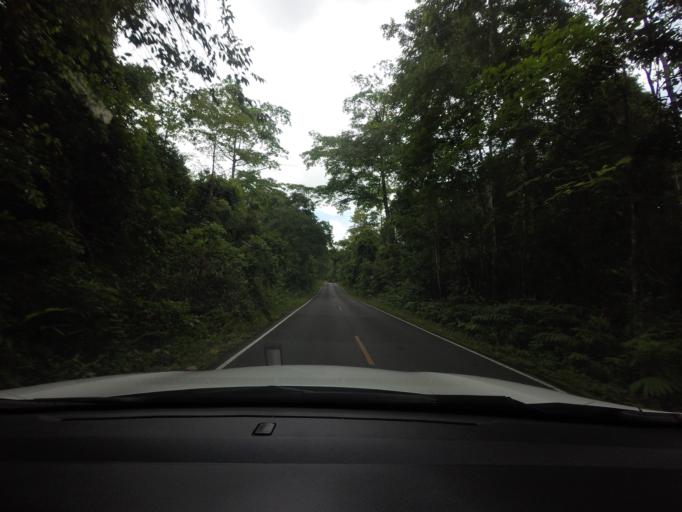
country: TH
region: Nakhon Nayok
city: Pak Phli
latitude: 14.2777
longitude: 101.3858
